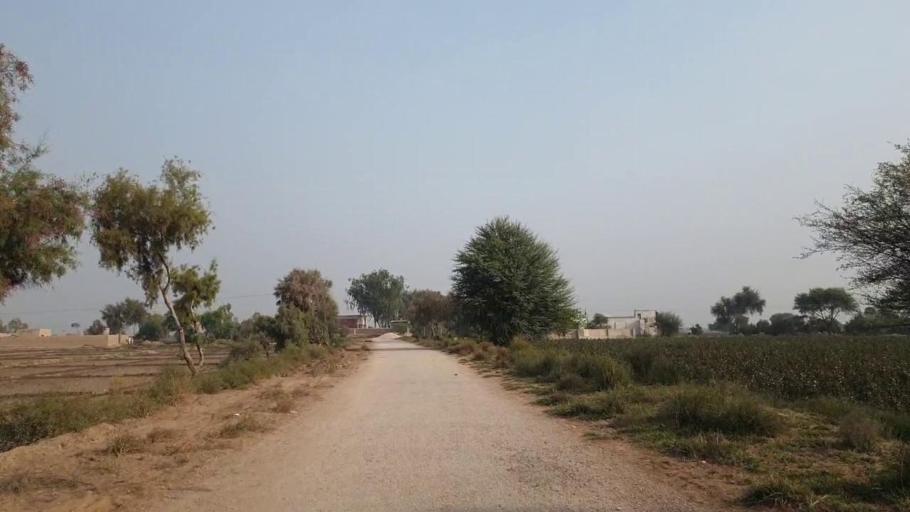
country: PK
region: Sindh
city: Bhan
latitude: 26.4741
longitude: 67.7249
